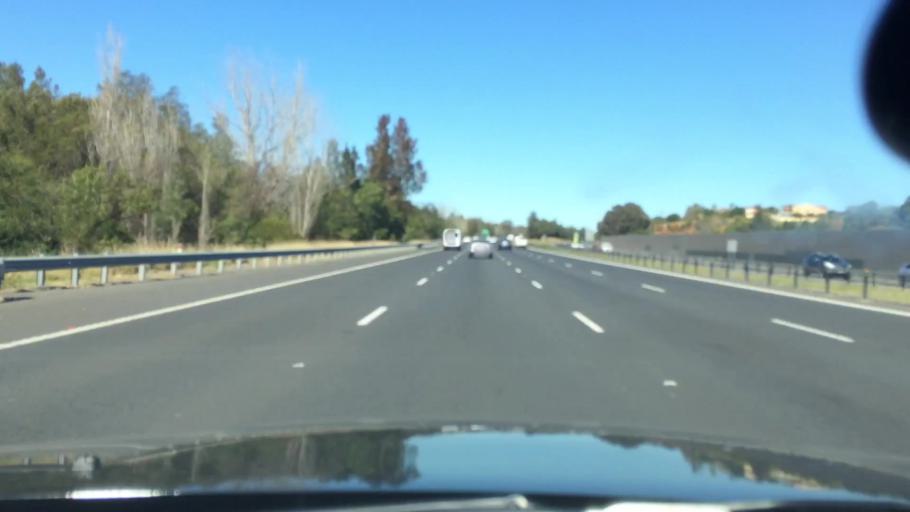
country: AU
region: New South Wales
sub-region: Campbelltown Municipality
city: Denham Court
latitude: -33.9926
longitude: 150.8523
